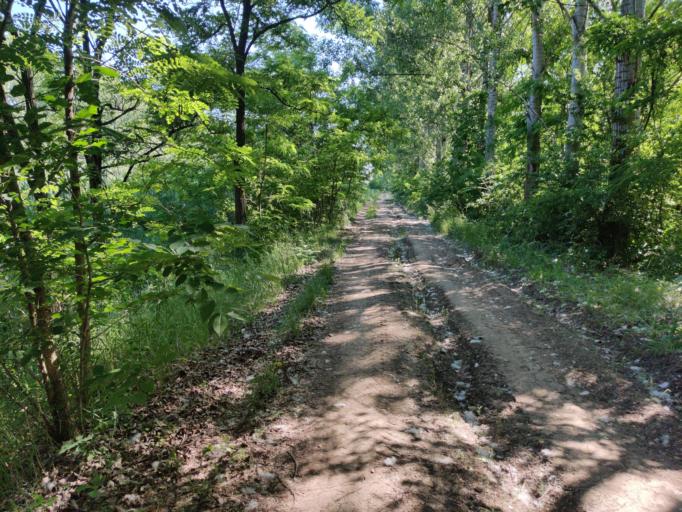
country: HU
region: Hajdu-Bihar
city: Balmazujvaros
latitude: 47.5830
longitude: 21.3529
